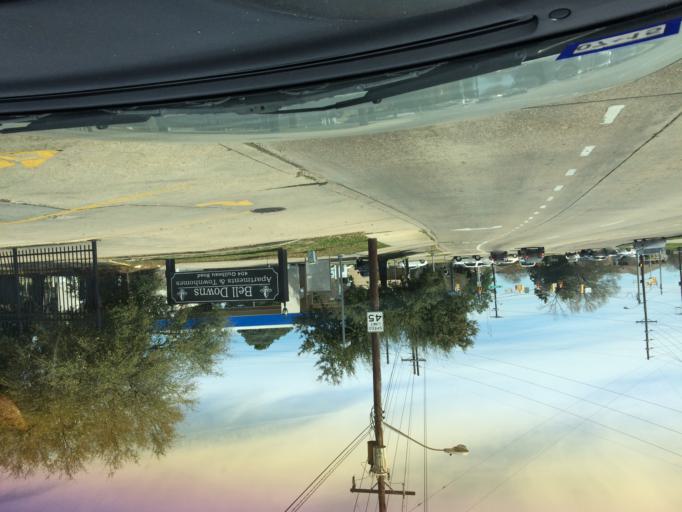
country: US
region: Louisiana
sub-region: Lafayette Parish
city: Scott
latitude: 30.1977
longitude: -92.0692
